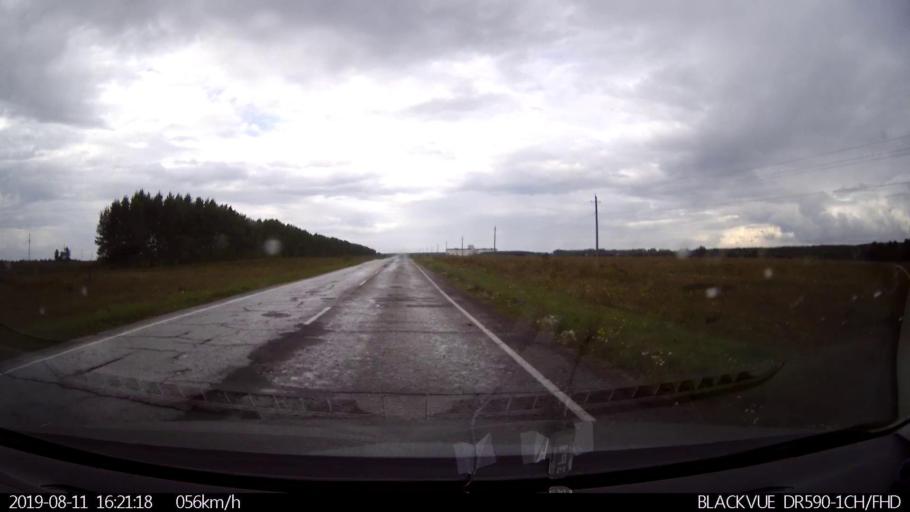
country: RU
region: Ulyanovsk
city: Mayna
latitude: 54.0788
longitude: 47.5986
